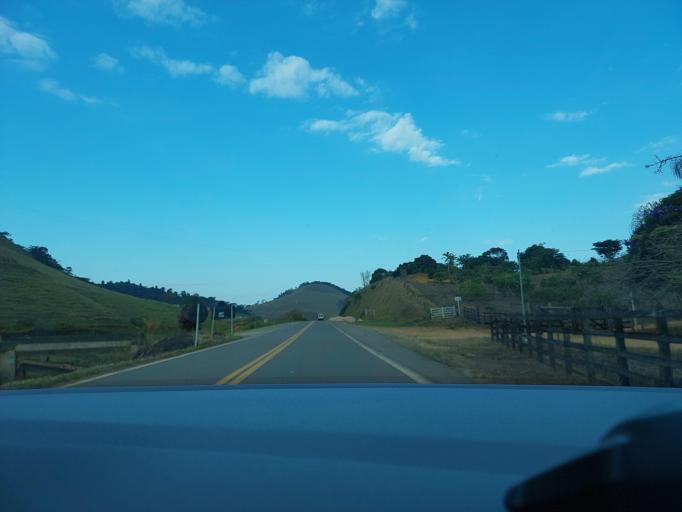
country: BR
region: Minas Gerais
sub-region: Muriae
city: Muriae
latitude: -21.0508
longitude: -42.5151
